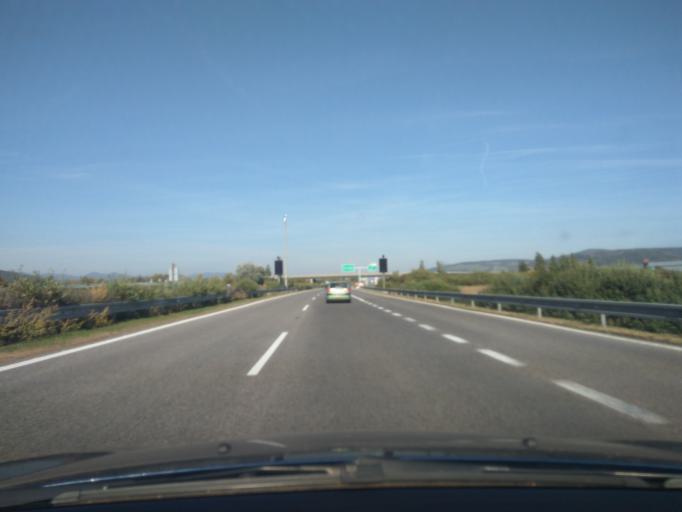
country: SK
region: Trenciansky
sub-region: Okres Nove Mesto nad Vahom
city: Nove Mesto nad Vahom
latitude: 48.7592
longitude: 17.8651
